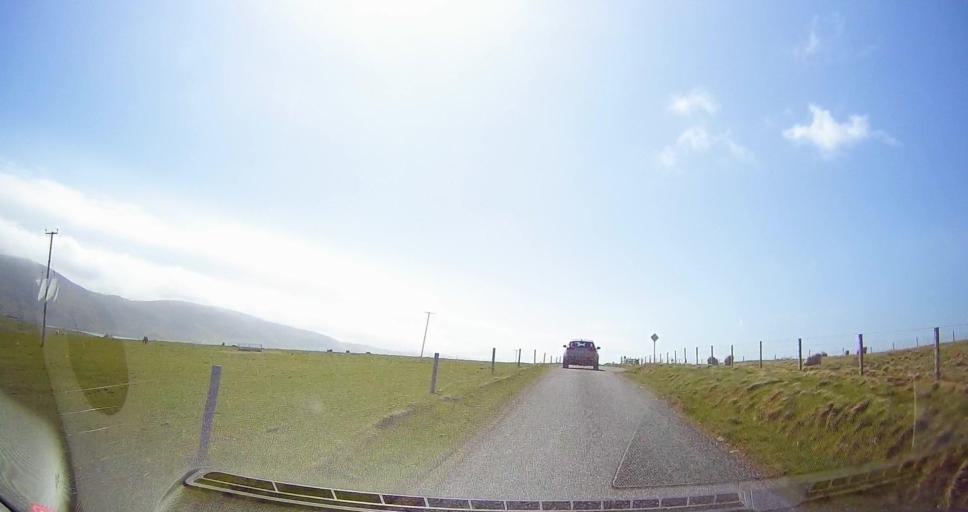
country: GB
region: Scotland
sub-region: Shetland Islands
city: Sandwick
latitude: 60.0759
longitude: -1.3383
